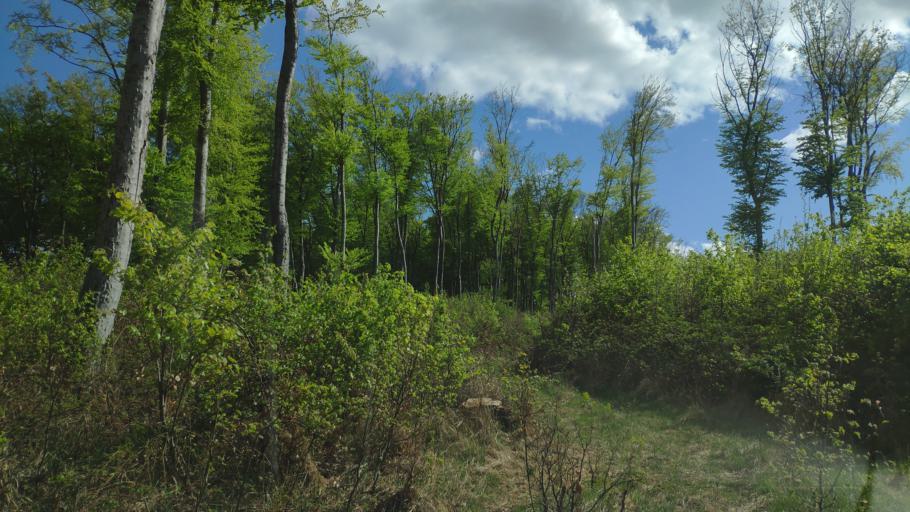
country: SK
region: Kosicky
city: Kosice
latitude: 48.6656
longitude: 21.4510
